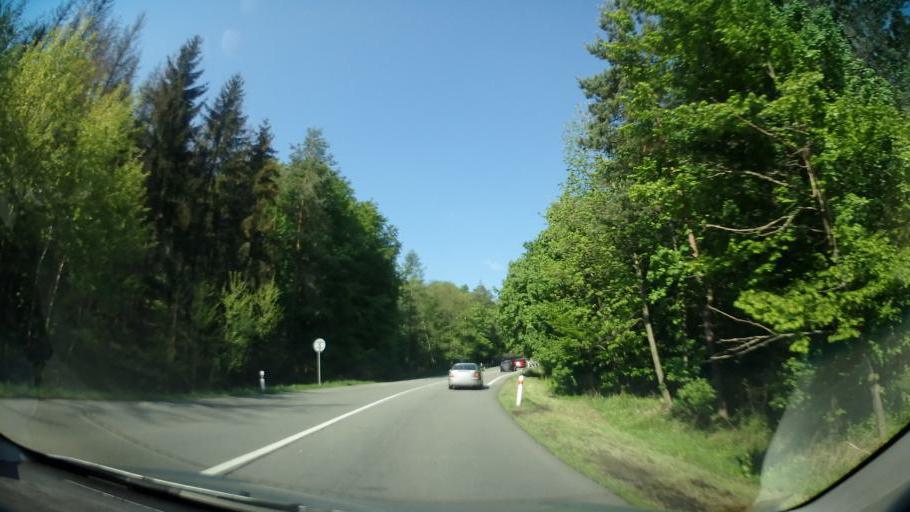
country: CZ
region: South Moravian
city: Zastavka
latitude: 49.1860
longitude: 16.3428
